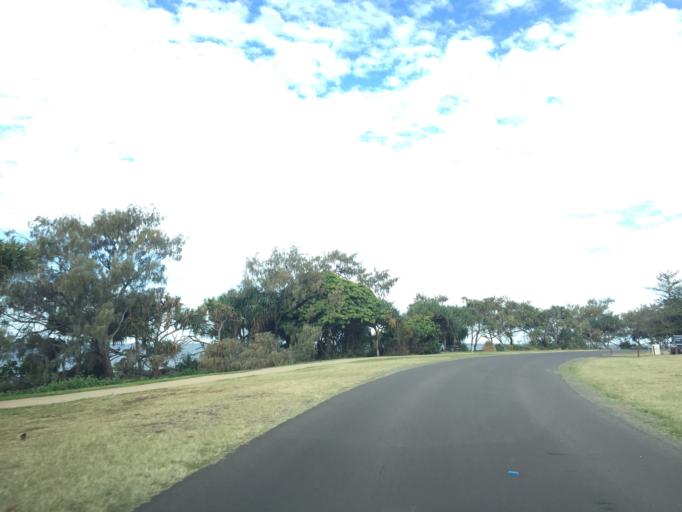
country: AU
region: Queensland
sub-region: Bundaberg
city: Bundaberg
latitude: -24.8156
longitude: 152.4670
